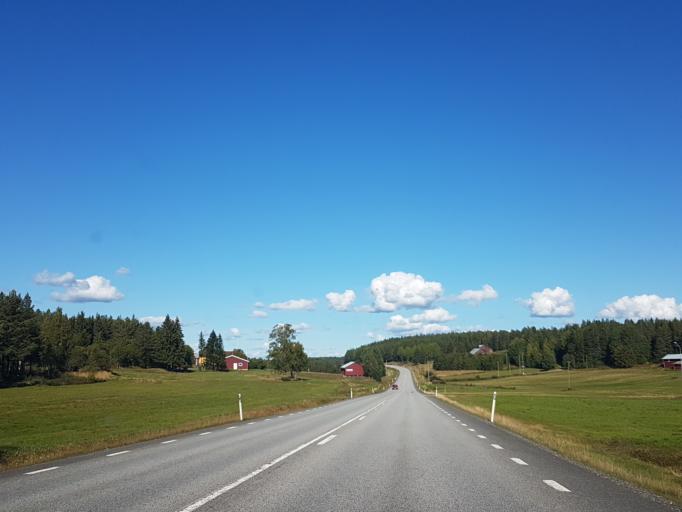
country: SE
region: Vaesterbotten
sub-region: Robertsfors Kommun
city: Robertsfors
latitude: 64.2082
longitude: 21.0173
